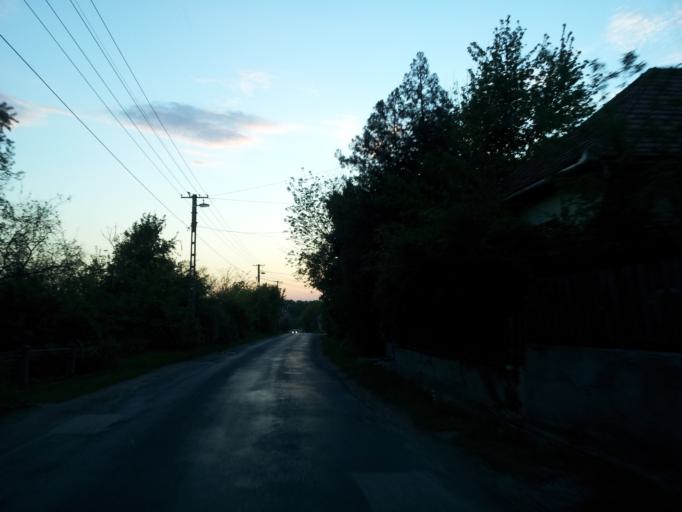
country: HU
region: Komarom-Esztergom
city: Csolnok
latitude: 47.6422
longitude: 18.7418
